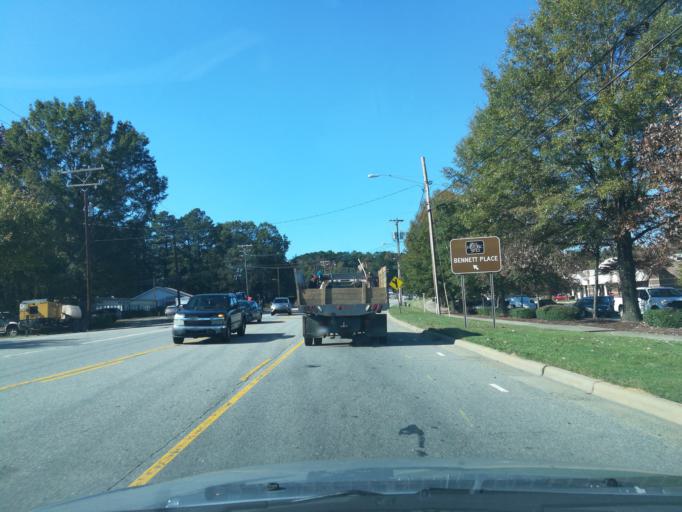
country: US
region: North Carolina
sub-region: Durham County
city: Durham
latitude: 36.0231
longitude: -78.9548
